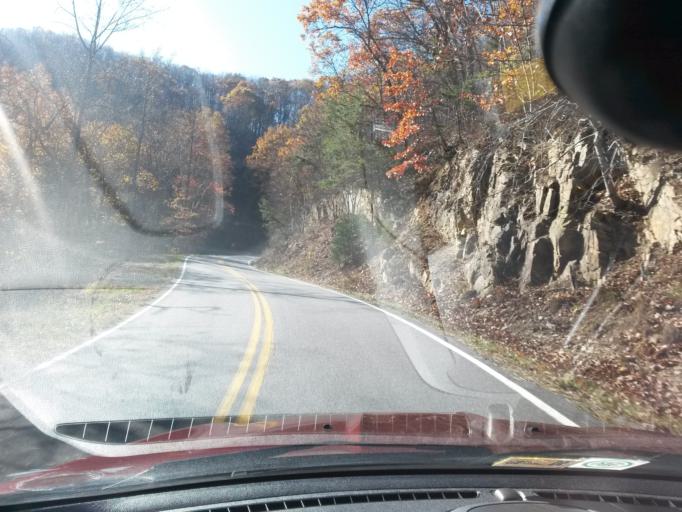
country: US
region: Virginia
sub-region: Botetourt County
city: Buchanan
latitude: 37.5022
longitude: -79.6661
